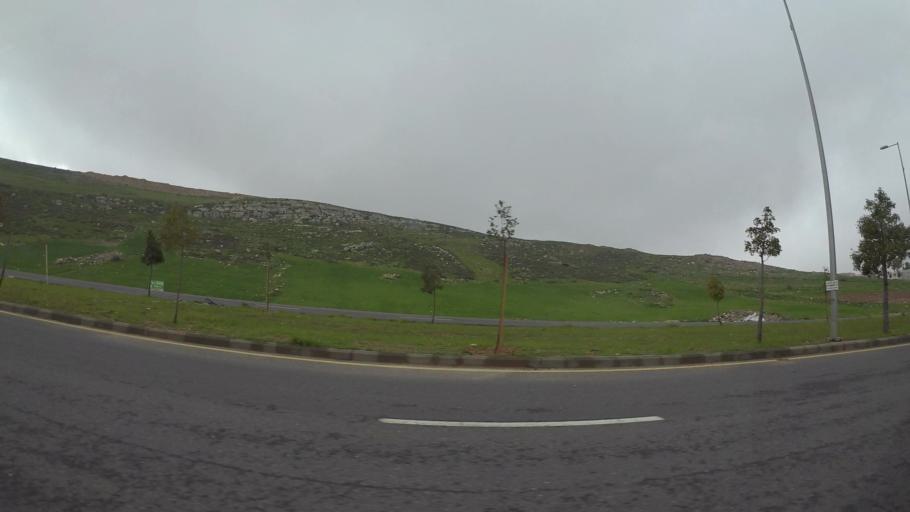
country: JO
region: Amman
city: Al Bunayyat ash Shamaliyah
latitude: 31.9319
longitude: 35.8760
